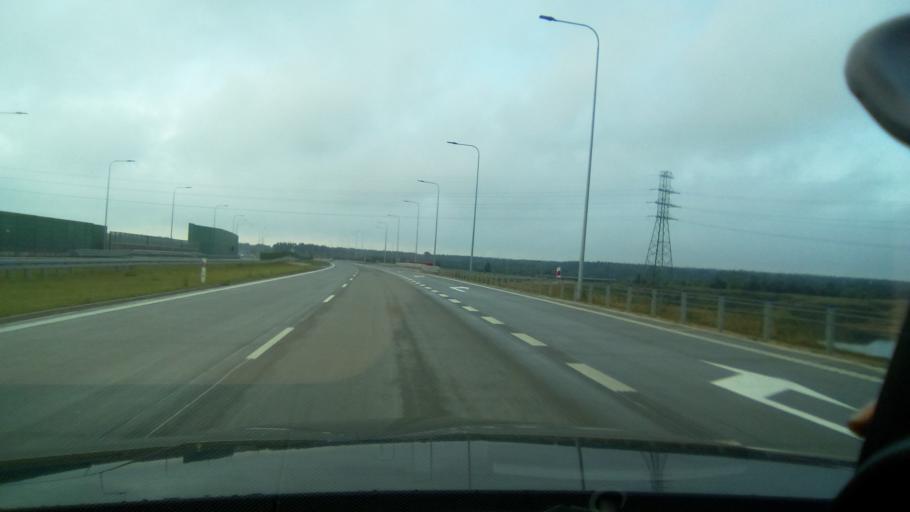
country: PL
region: Silesian Voivodeship
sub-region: Powiat czestochowski
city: Blachownia
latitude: 50.7825
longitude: 19.0030
